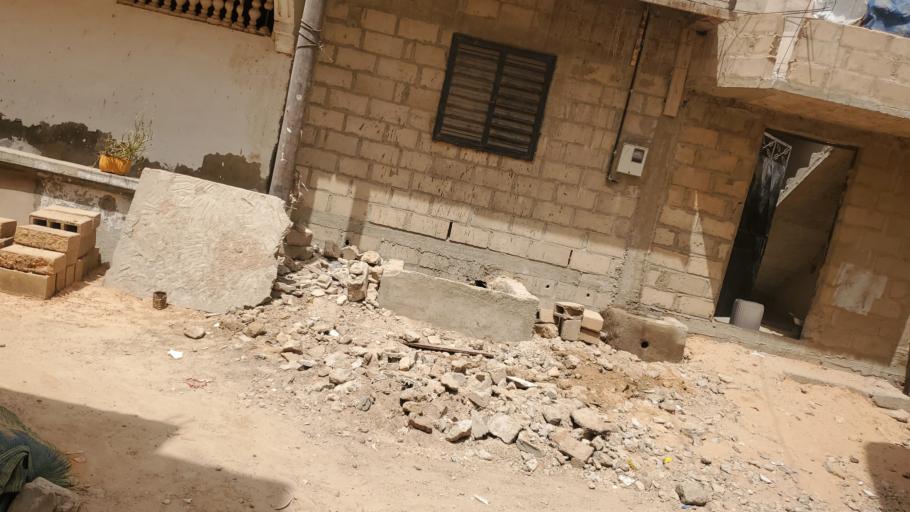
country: SN
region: Saint-Louis
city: Saint-Louis
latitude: 16.0173
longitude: -16.4853
